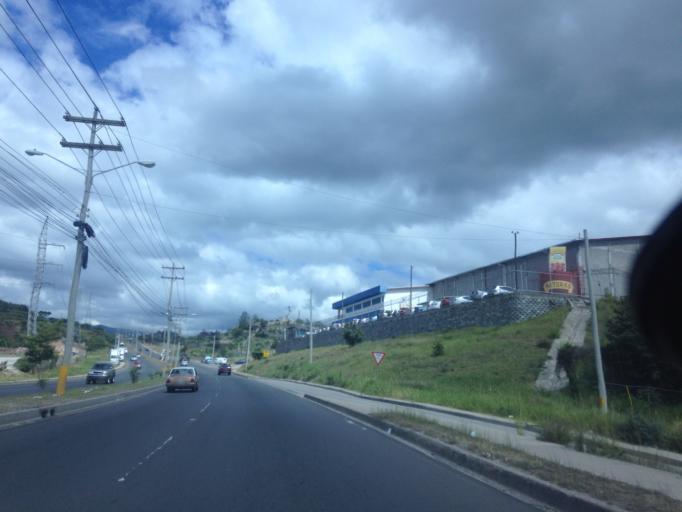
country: HN
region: Francisco Morazan
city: Yaguacire
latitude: 14.0455
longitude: -87.2433
